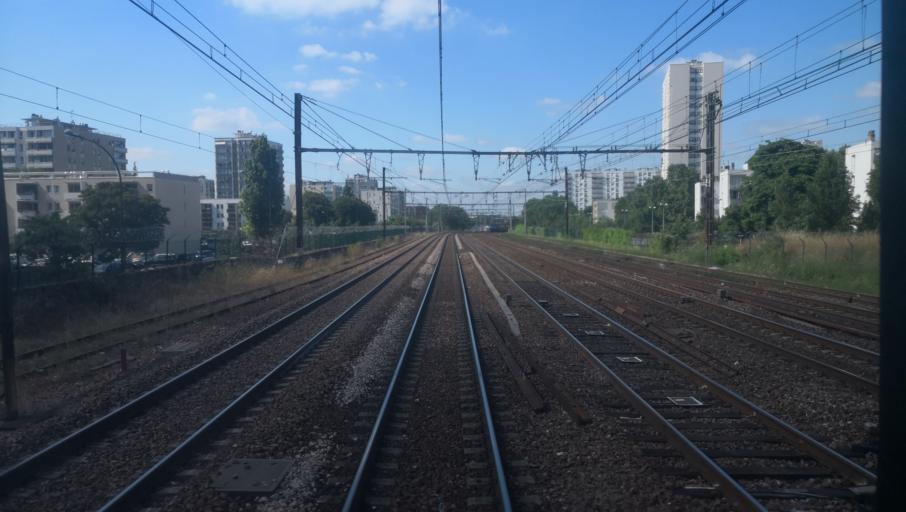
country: FR
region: Ile-de-France
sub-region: Departement du Val-de-Marne
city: Alfortville
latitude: 48.7910
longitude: 2.4310
